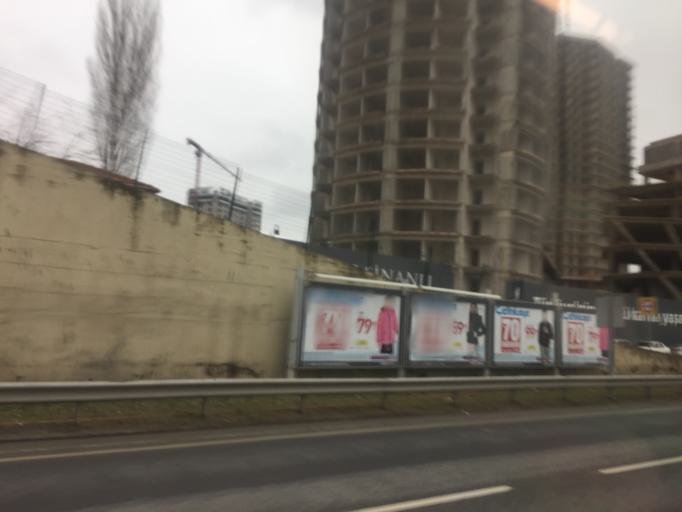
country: TR
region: Istanbul
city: UEskuedar
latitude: 40.9942
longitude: 29.0496
